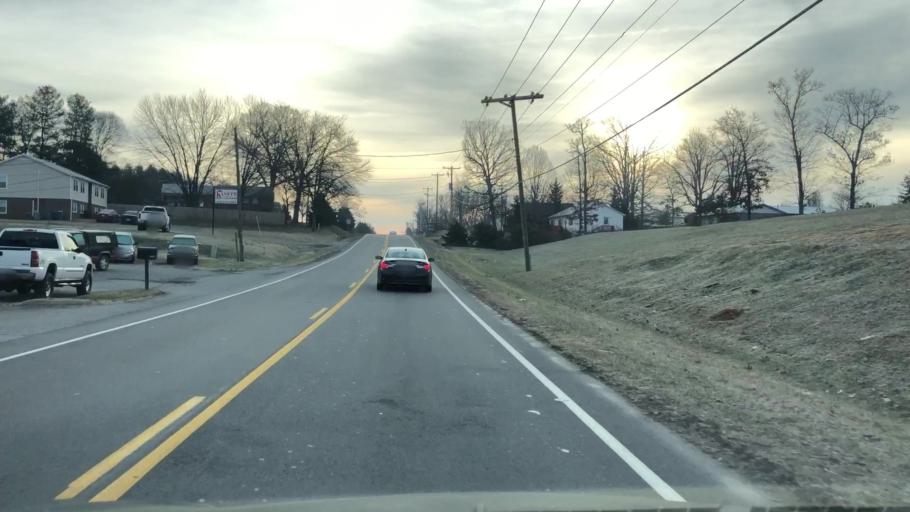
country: US
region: Virginia
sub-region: Campbell County
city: Timberlake
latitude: 37.3336
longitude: -79.2606
